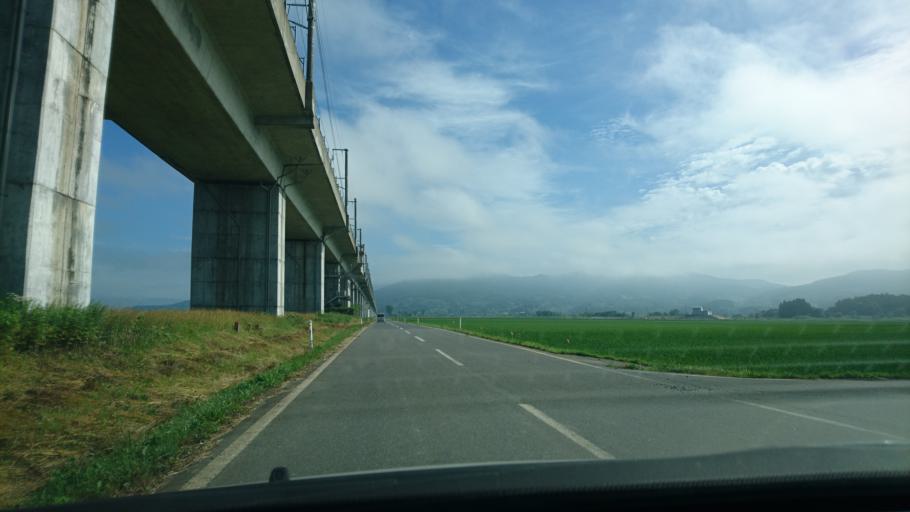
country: JP
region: Iwate
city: Ichinoseki
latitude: 38.9520
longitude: 141.1490
